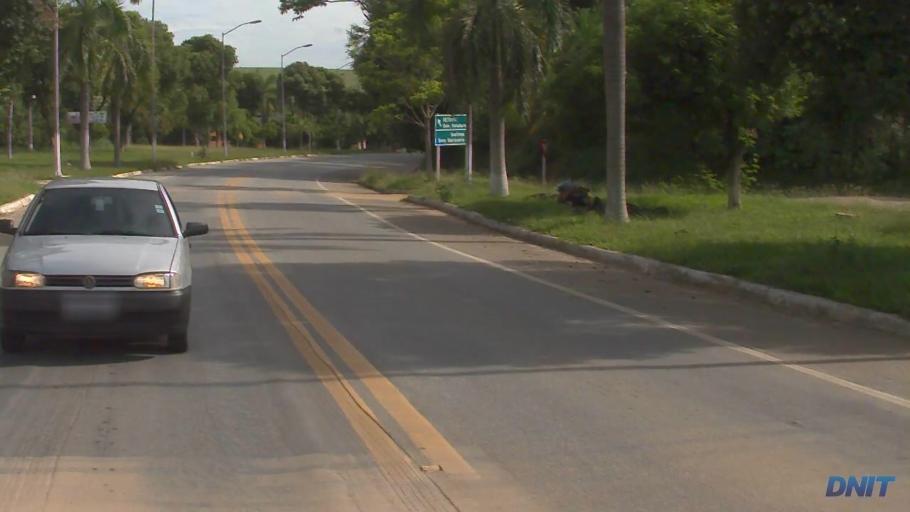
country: BR
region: Minas Gerais
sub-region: Belo Oriente
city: Belo Oriente
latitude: -19.2332
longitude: -42.3290
